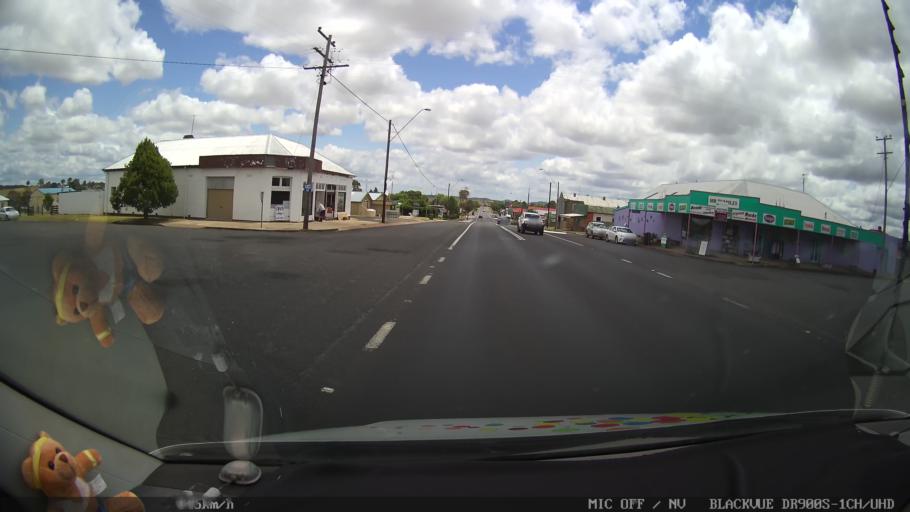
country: AU
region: New South Wales
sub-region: Glen Innes Severn
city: Glen Innes
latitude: -29.4426
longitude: 151.8460
